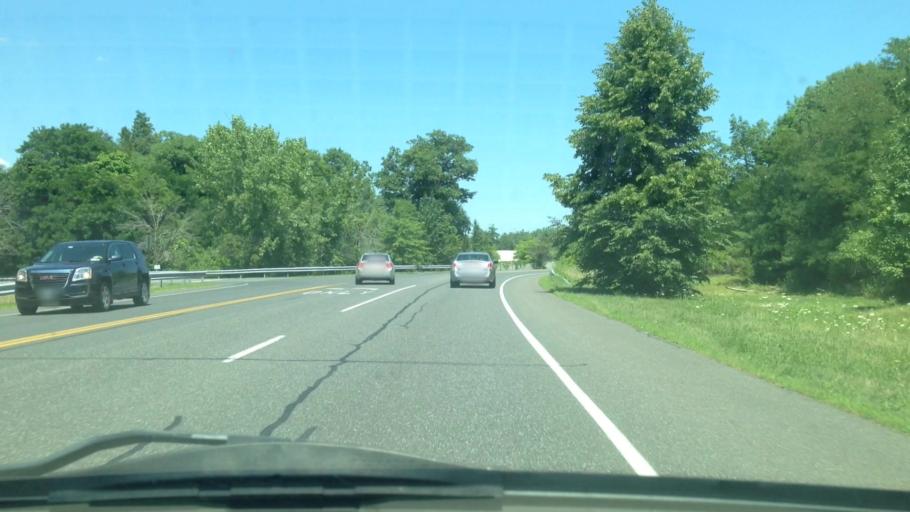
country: US
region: New York
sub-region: Ulster County
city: Lincoln Park
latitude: 41.9626
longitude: -73.9835
